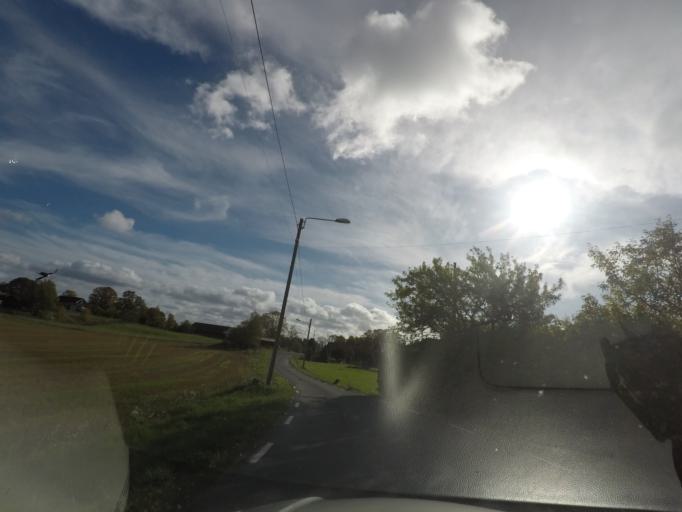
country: SE
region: Soedermanland
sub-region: Eskilstuna Kommun
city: Kvicksund
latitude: 59.3167
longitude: 16.2478
